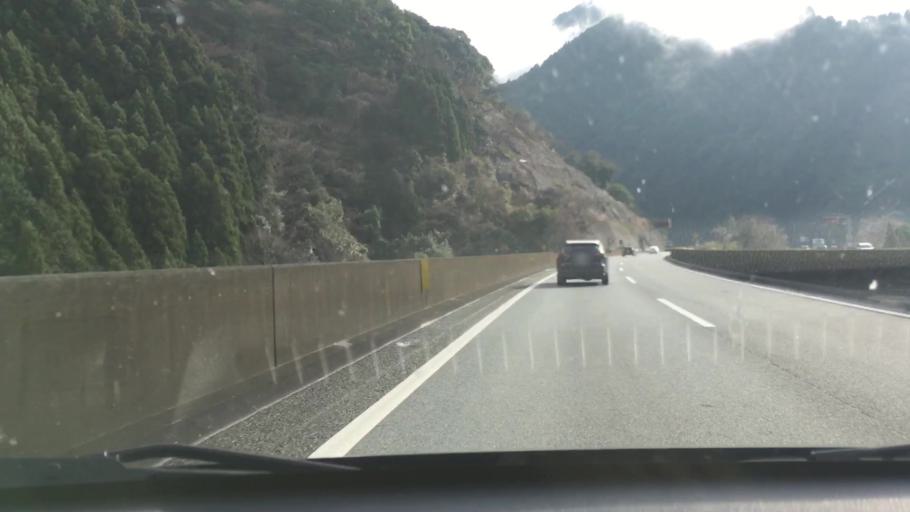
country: JP
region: Kumamoto
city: Yatsushiro
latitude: 32.4284
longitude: 130.7025
